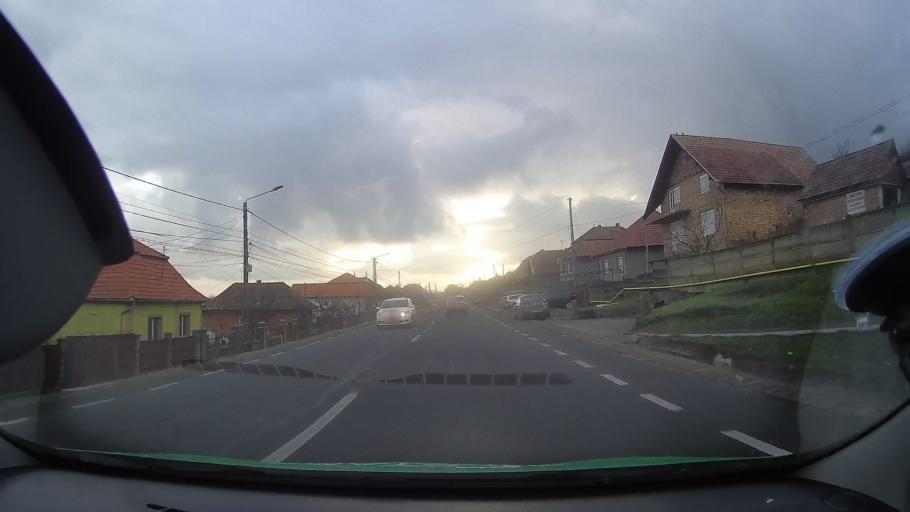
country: RO
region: Cluj
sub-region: Comuna Viisoara
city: Viisoara
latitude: 46.5075
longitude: 23.9194
